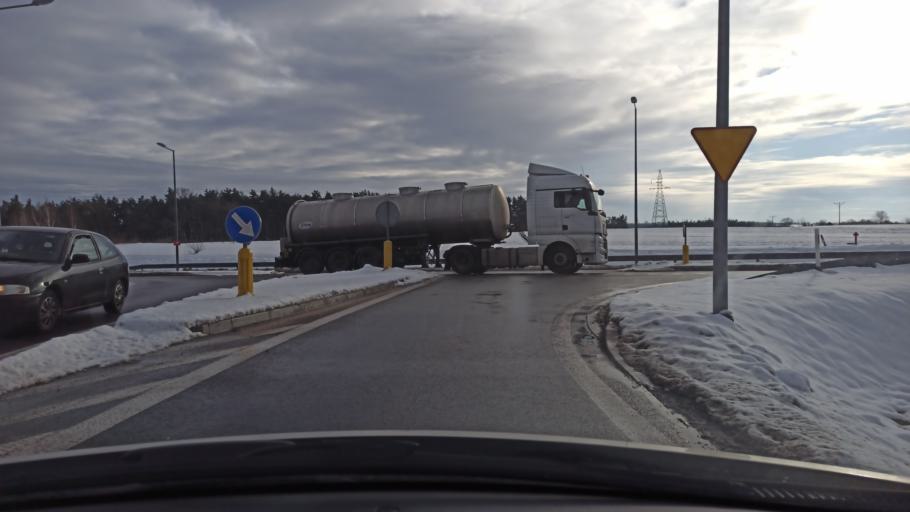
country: PL
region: Subcarpathian Voivodeship
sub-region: Powiat lezajski
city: Wierzawice
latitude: 50.2418
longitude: 22.4382
